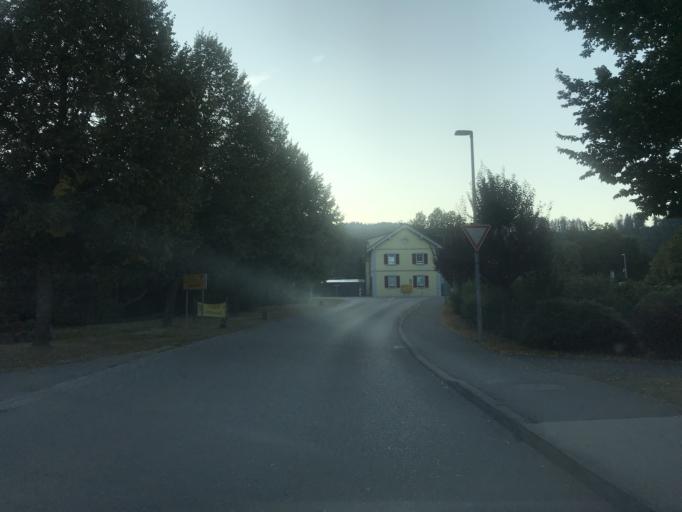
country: DE
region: Baden-Wuerttemberg
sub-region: Freiburg Region
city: Hausen
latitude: 47.6797
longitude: 7.8450
